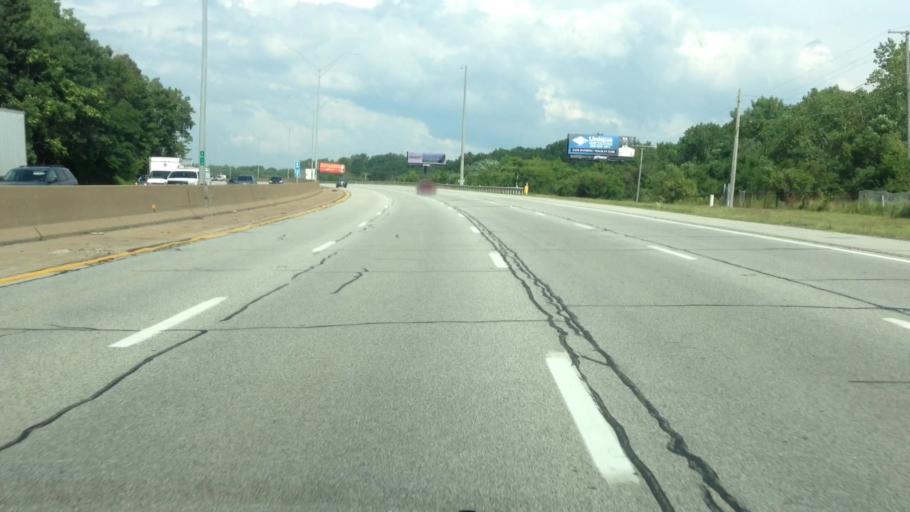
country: US
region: Ohio
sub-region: Cuyahoga County
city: Brooklyn
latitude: 41.4457
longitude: -81.7616
